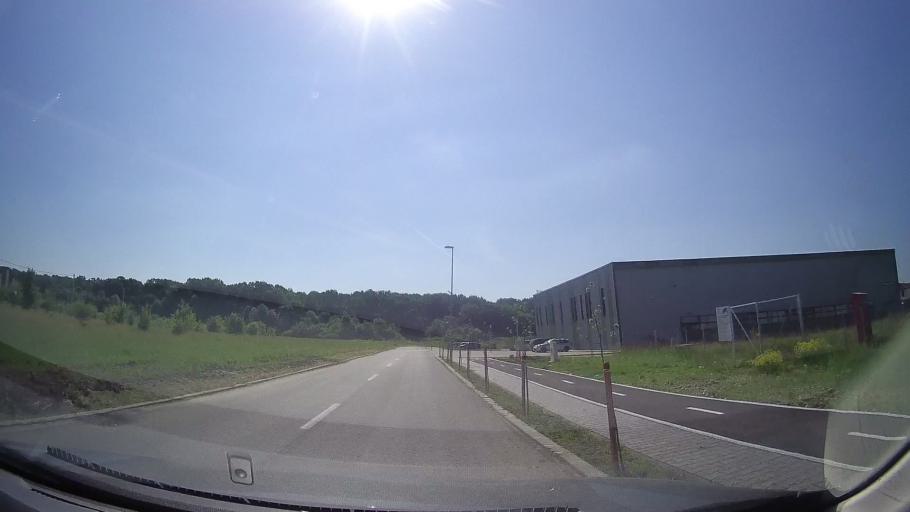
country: RO
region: Timis
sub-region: Comuna Dumbravita
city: Dumbravita
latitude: 45.7975
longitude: 21.2554
